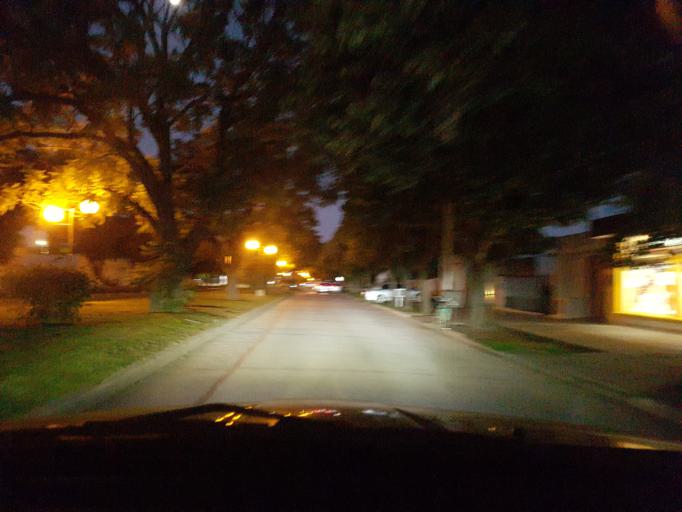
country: AR
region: Cordoba
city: General Cabrera
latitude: -32.7598
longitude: -63.7867
